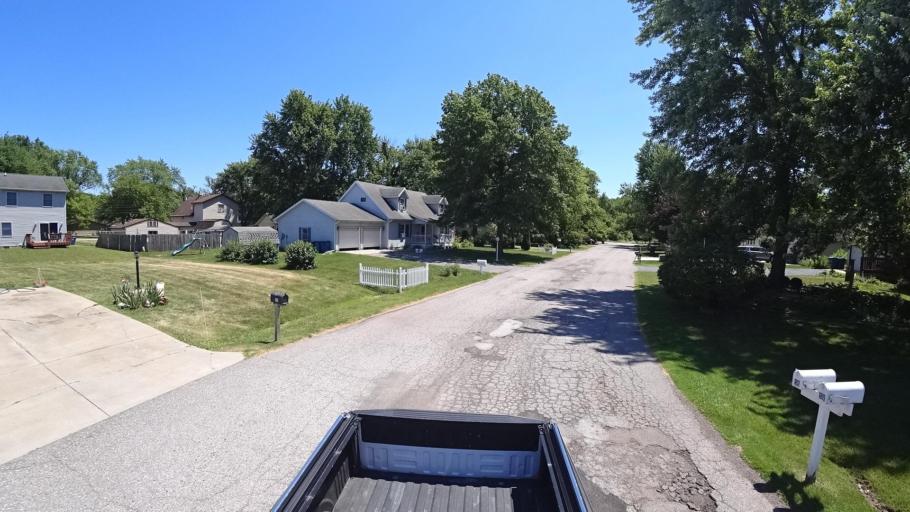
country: US
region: Indiana
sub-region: Porter County
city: Porter
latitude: 41.6104
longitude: -87.0780
